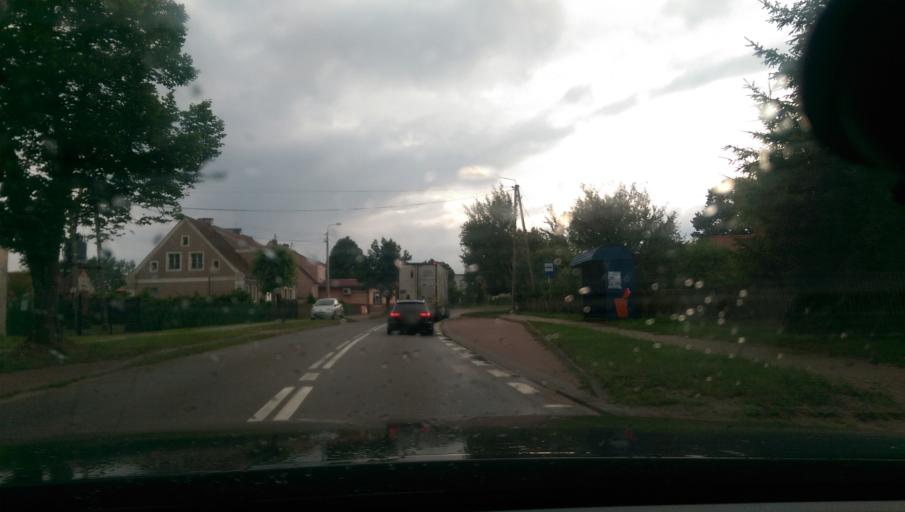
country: PL
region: Warmian-Masurian Voivodeship
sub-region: Powiat szczycienski
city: Swietajno
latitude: 53.5572
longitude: 21.1126
